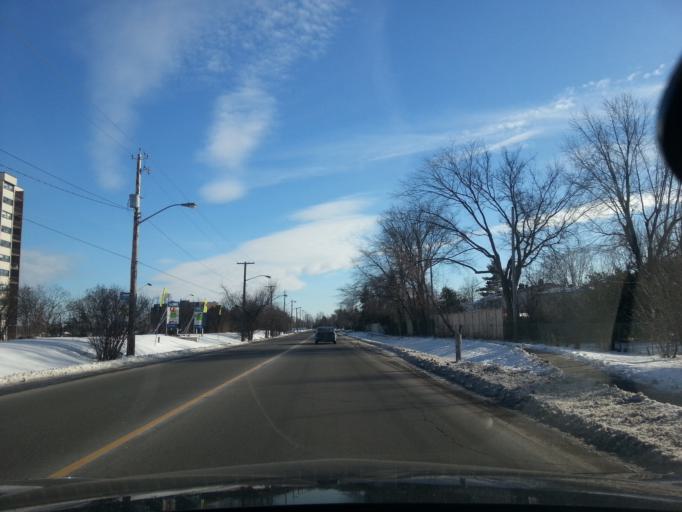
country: CA
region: Ontario
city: Ottawa
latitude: 45.3978
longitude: -75.6175
